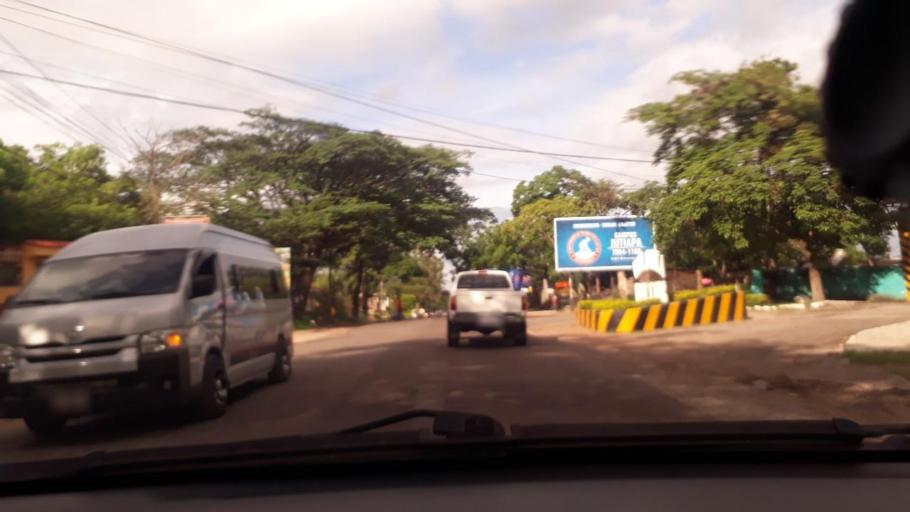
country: GT
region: Jutiapa
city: Jutiapa
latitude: 14.2905
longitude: -89.9268
